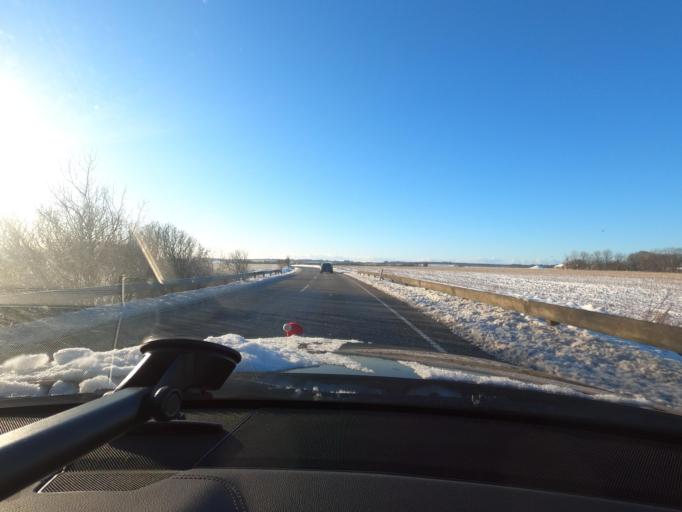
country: DK
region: South Denmark
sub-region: Tonder Kommune
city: Toftlund
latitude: 55.1770
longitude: 8.9984
